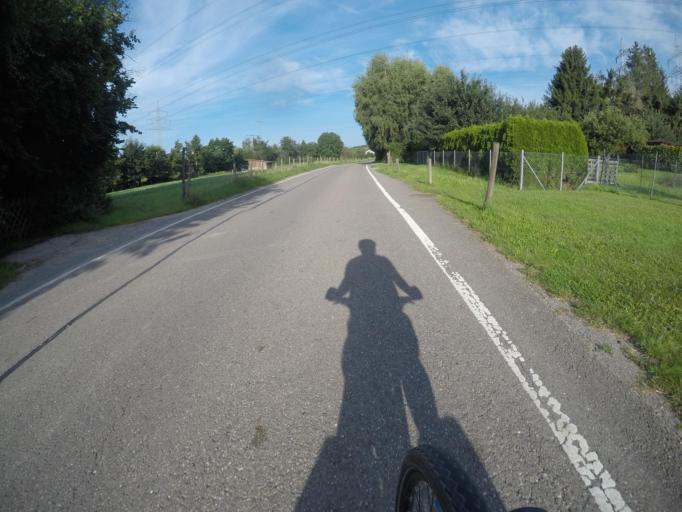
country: DE
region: Baden-Wuerttemberg
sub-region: Regierungsbezirk Stuttgart
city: Leonberg
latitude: 48.7920
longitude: 8.9805
